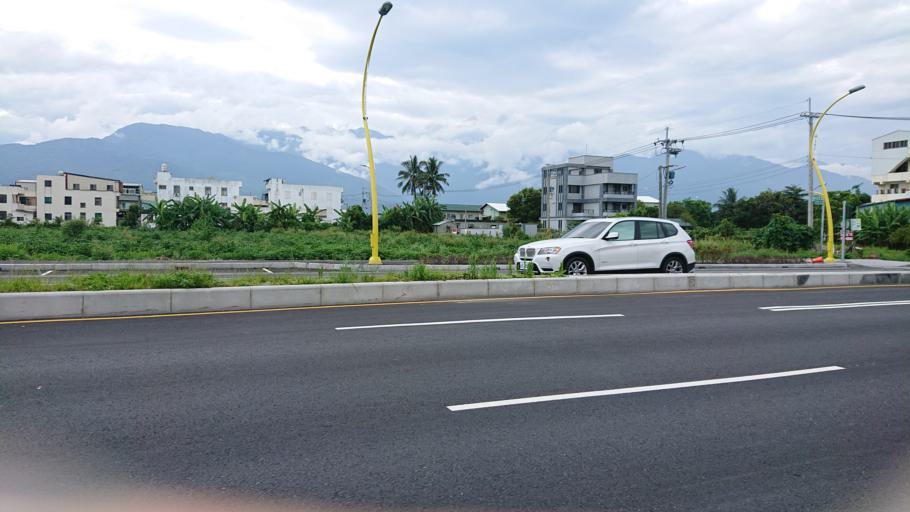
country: TW
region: Taiwan
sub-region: Hualien
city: Hualian
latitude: 23.9510
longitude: 121.5995
